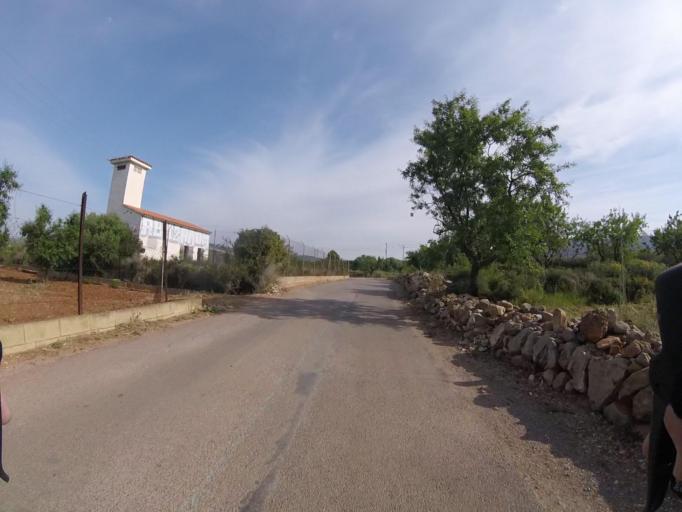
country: ES
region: Valencia
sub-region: Provincia de Castello
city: Alcoceber
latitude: 40.2658
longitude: 0.2530
